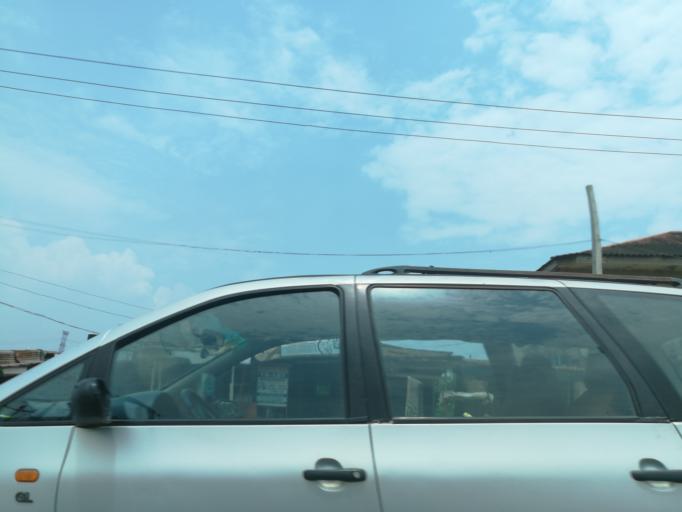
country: NG
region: Lagos
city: Ikorodu
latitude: 6.5979
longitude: 3.5885
